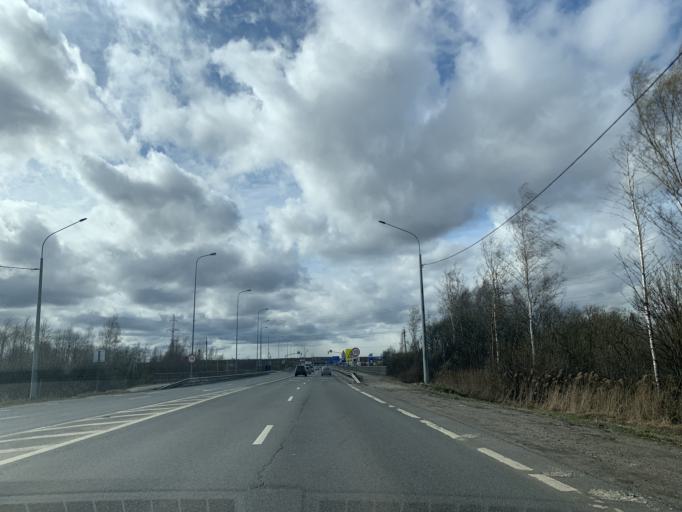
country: RU
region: Jaroslavl
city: Yaroslavl
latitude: 57.6829
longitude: 39.9147
